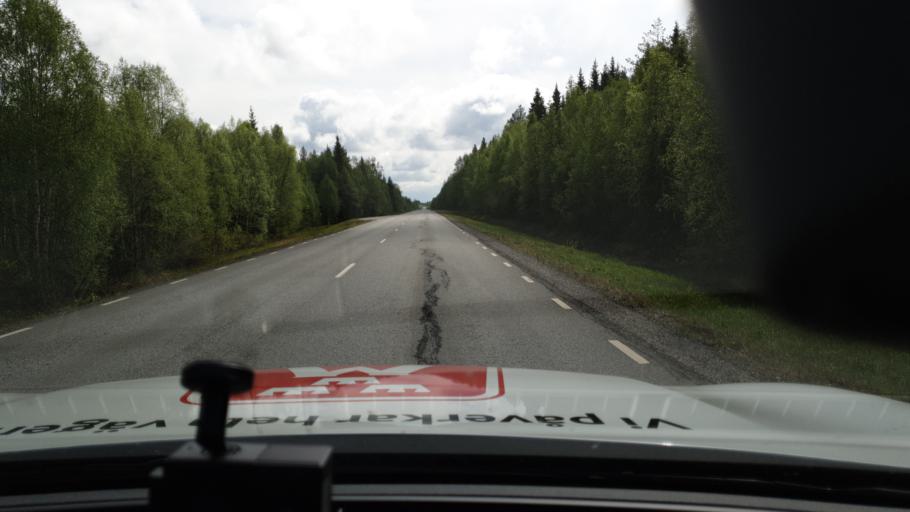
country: SE
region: Vaesterbotten
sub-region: Lycksele Kommun
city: Lycksele
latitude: 64.7086
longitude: 18.6961
